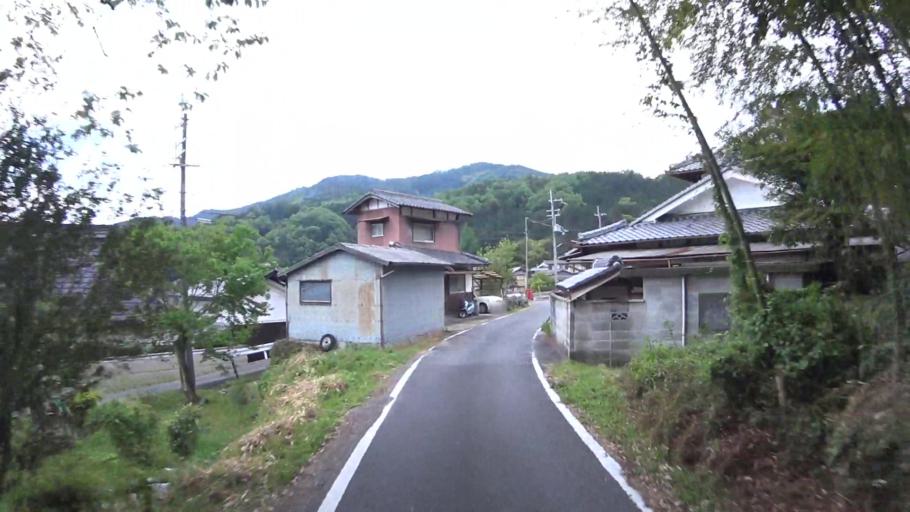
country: JP
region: Kyoto
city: Kameoka
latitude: 35.0543
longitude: 135.5303
